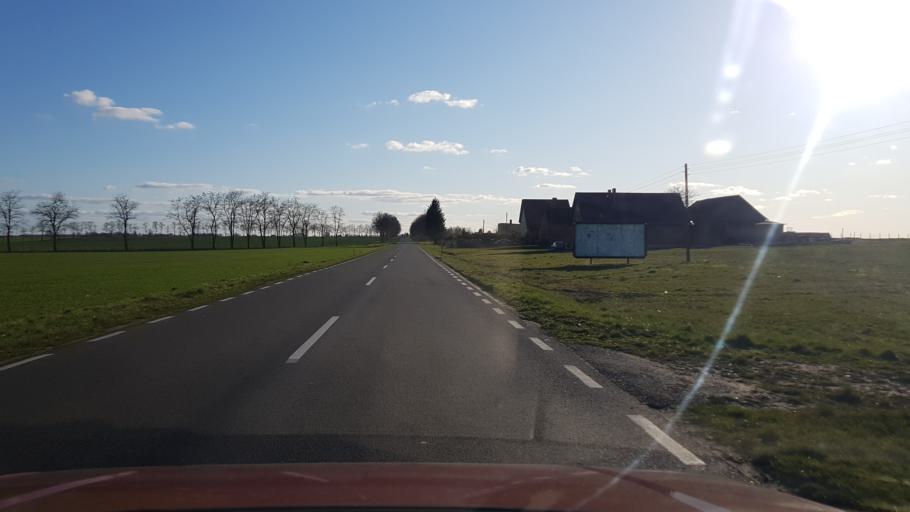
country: PL
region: West Pomeranian Voivodeship
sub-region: Powiat stargardzki
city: Stargard Szczecinski
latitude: 53.3680
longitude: 15.0707
